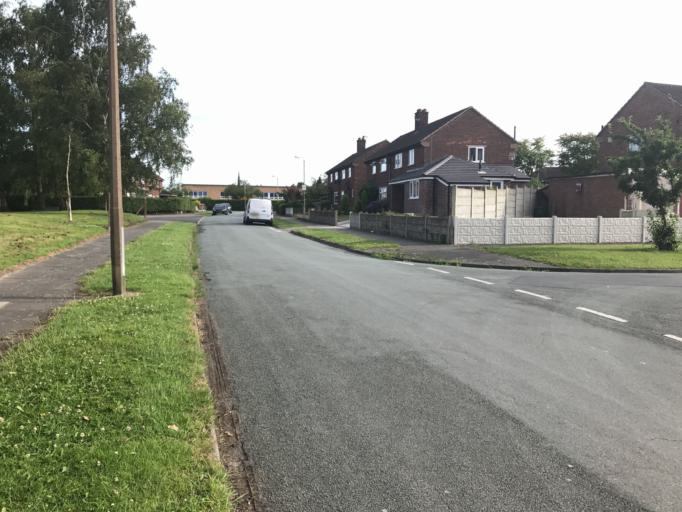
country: GB
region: England
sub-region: Cheshire West and Chester
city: Northwich
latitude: 53.2430
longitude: -2.5062
